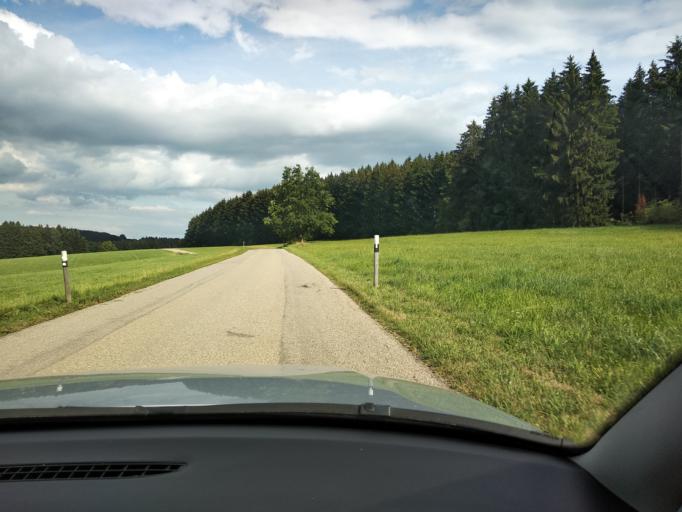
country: DE
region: Bavaria
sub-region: Swabia
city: Kronburg
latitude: 47.8995
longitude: 10.1671
